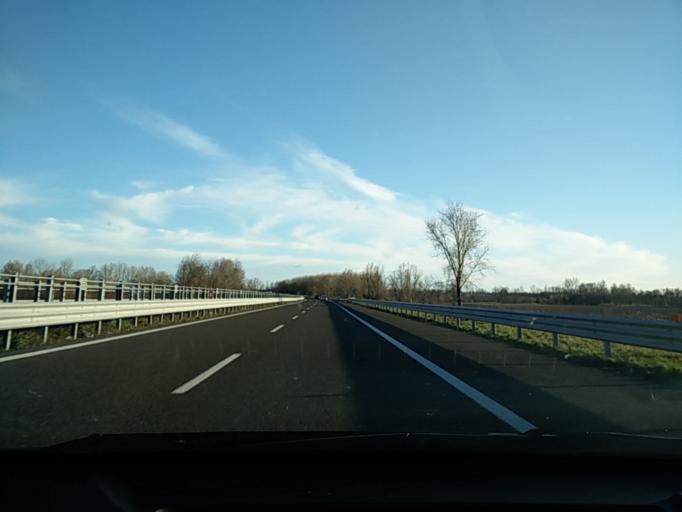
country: IT
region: Friuli Venezia Giulia
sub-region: Provincia di Udine
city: Buia
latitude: 46.2135
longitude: 13.0925
